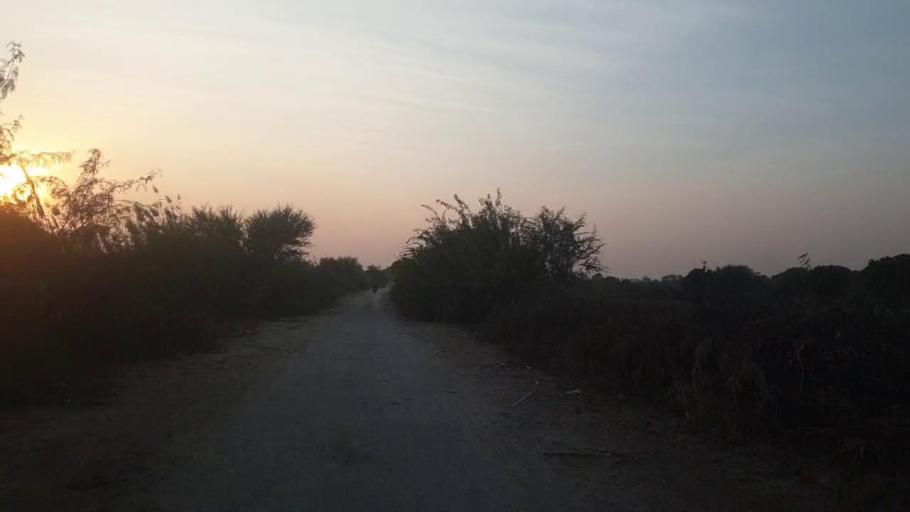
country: PK
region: Sindh
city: Tando Jam
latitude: 25.3830
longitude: 68.5768
